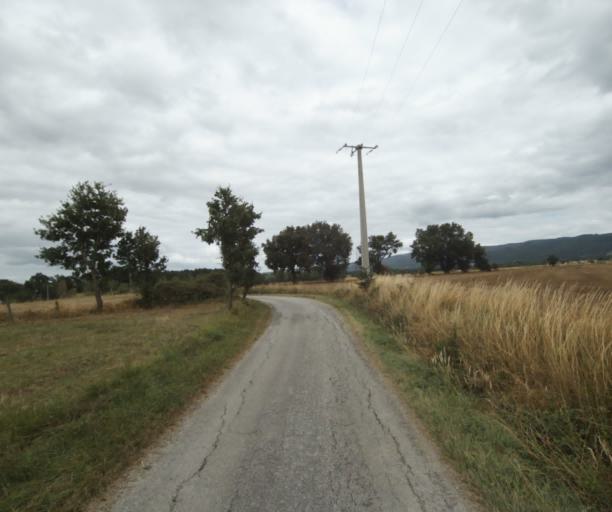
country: FR
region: Midi-Pyrenees
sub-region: Departement du Tarn
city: Soreze
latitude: 43.4761
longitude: 2.0478
